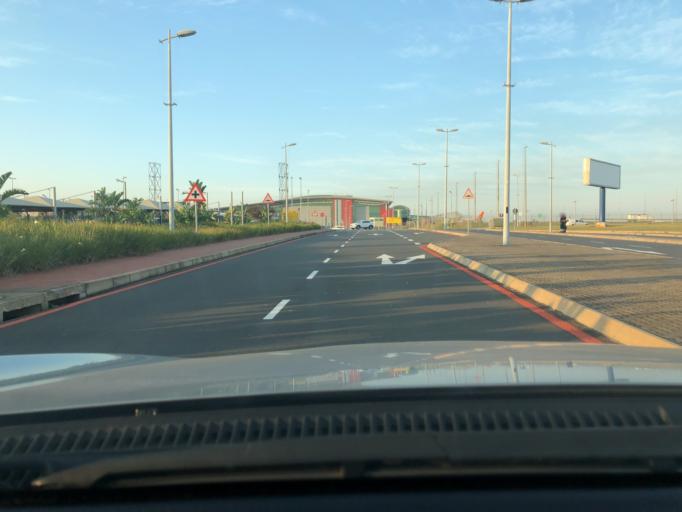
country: ZA
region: KwaZulu-Natal
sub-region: iLembe District Municipality
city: Ballitoville
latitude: -29.6232
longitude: 31.1018
